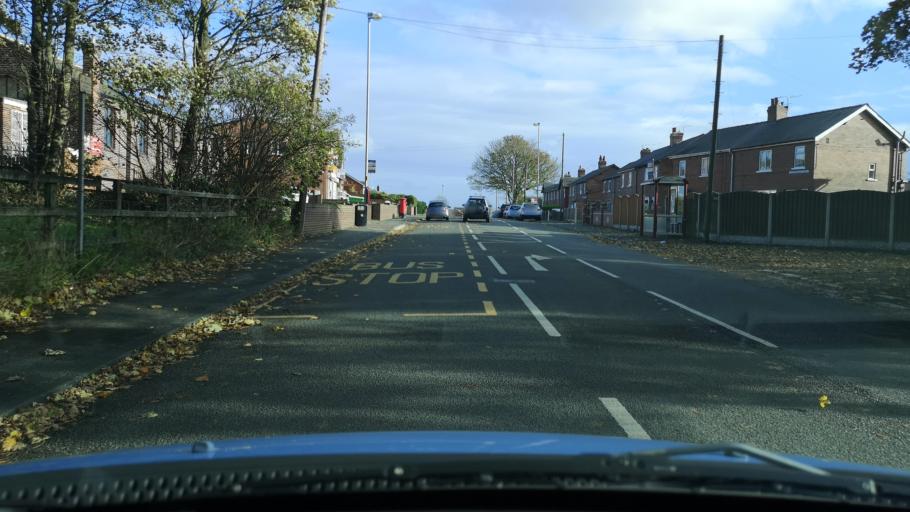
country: GB
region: England
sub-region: City and Borough of Wakefield
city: Crofton
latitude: 53.6524
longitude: -1.4208
